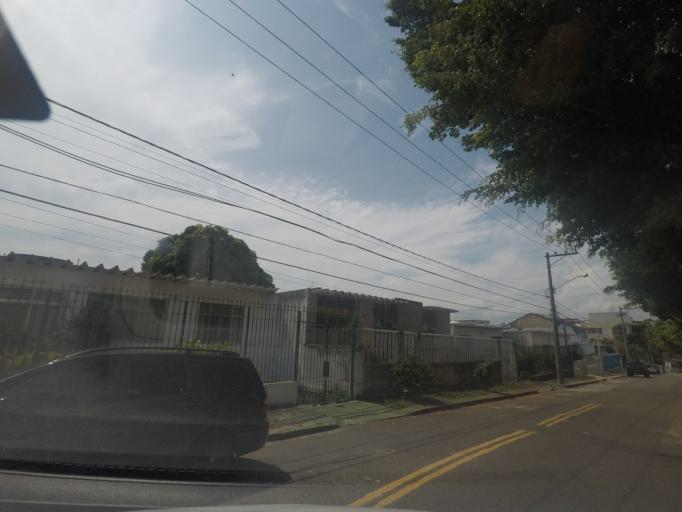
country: BR
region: Rio de Janeiro
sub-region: Rio De Janeiro
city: Rio de Janeiro
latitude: -22.8146
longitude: -43.2103
